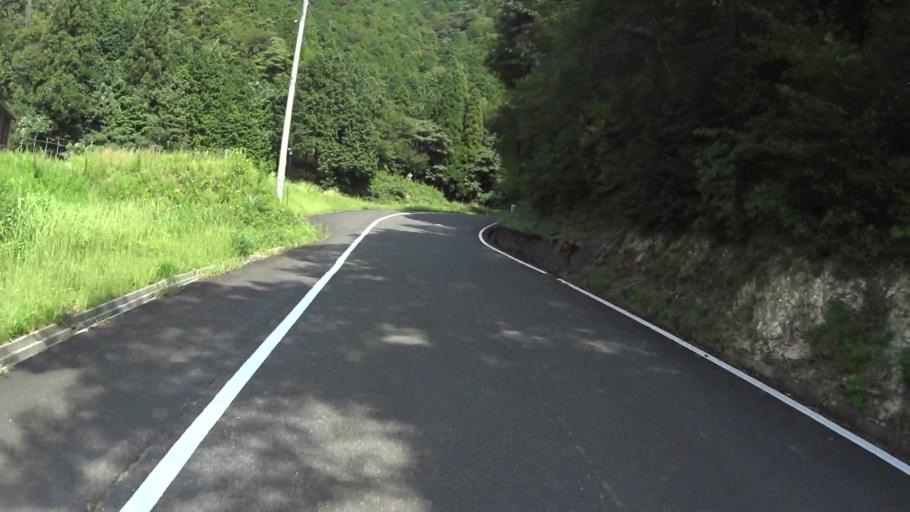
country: JP
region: Kyoto
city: Miyazu
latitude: 35.6764
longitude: 135.2707
